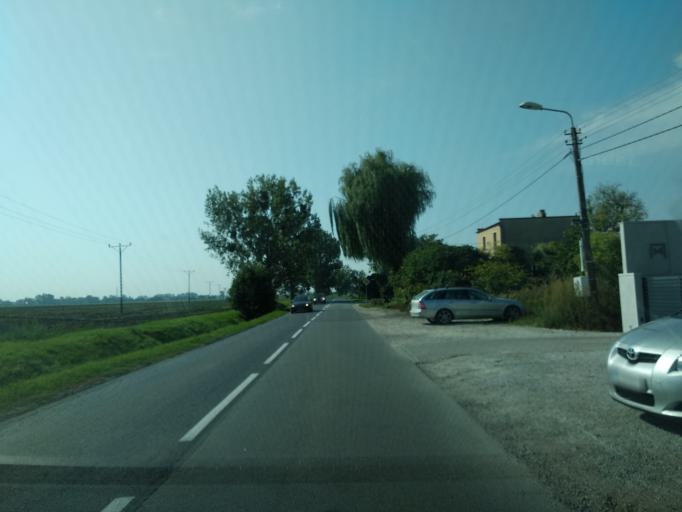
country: PL
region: Lower Silesian Voivodeship
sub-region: Powiat wroclawski
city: Zerniki Wroclawskie
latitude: 51.0477
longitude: 17.0302
